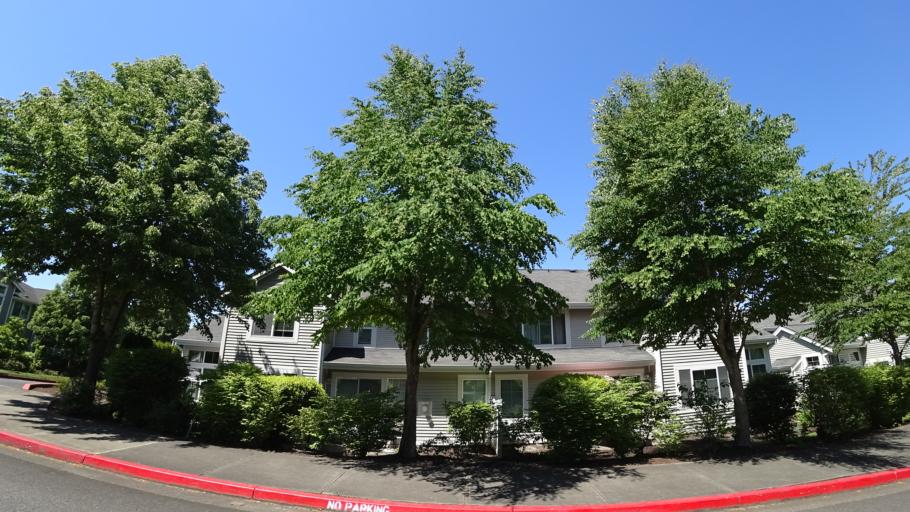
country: US
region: Oregon
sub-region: Washington County
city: Aloha
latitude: 45.4927
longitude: -122.8434
